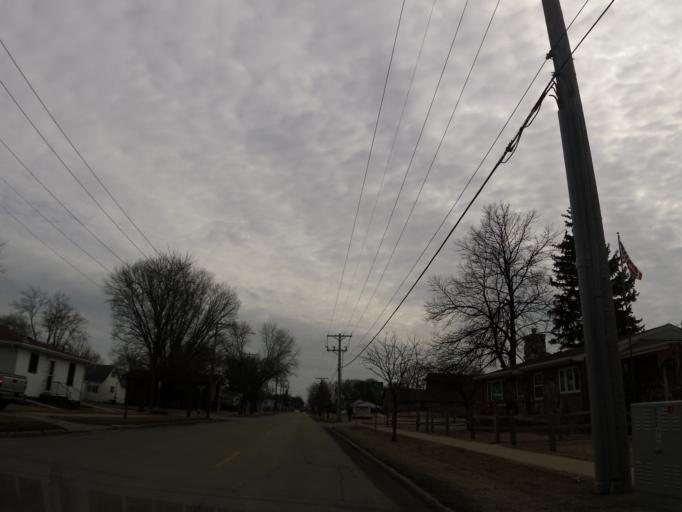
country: US
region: North Dakota
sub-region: Grand Forks County
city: Grand Forks
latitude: 47.9288
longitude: -97.0553
